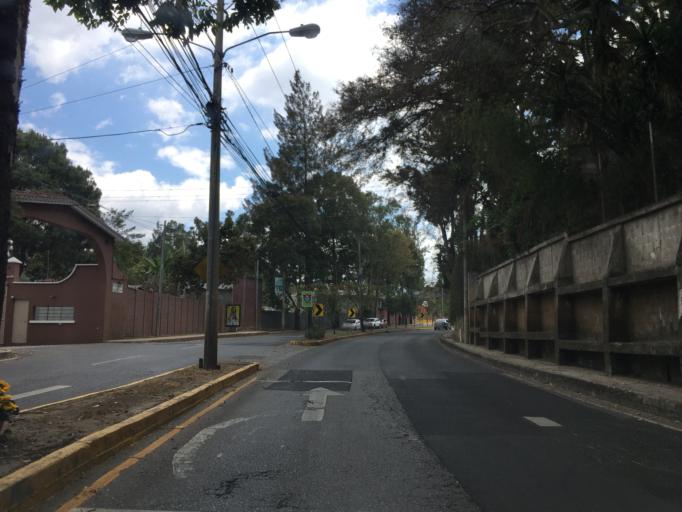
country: GT
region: Guatemala
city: Guatemala City
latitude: 14.6132
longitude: -90.4717
